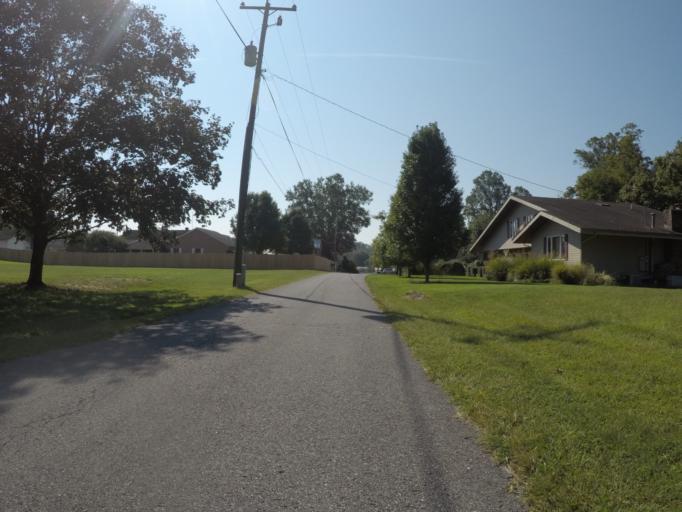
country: US
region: West Virginia
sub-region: Cabell County
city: Barboursville
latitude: 38.3723
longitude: -82.2764
